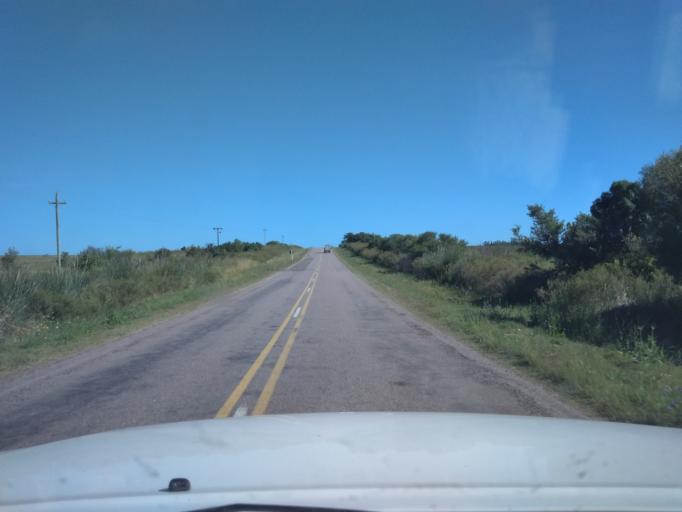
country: UY
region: Canelones
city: San Ramon
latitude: -34.1809
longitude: -55.9415
